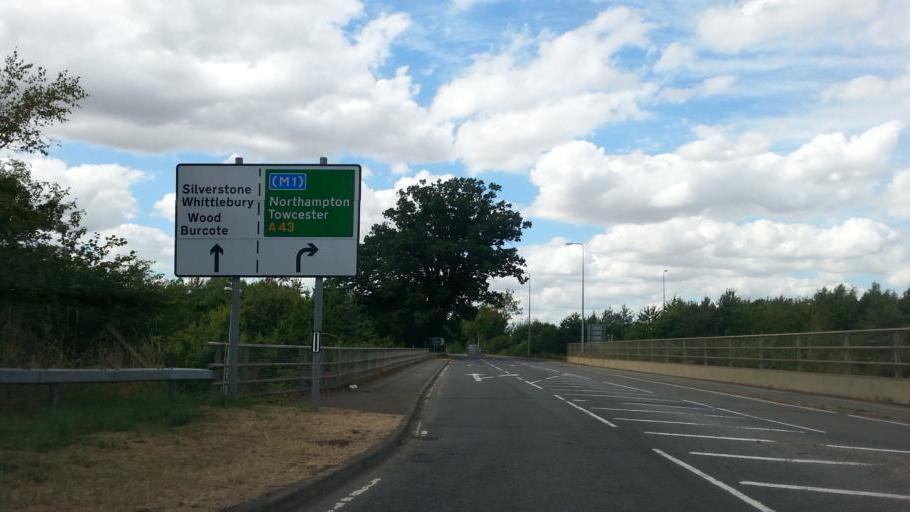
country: GB
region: England
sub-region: Northamptonshire
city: Silverstone
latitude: 52.0816
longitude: -1.0289
